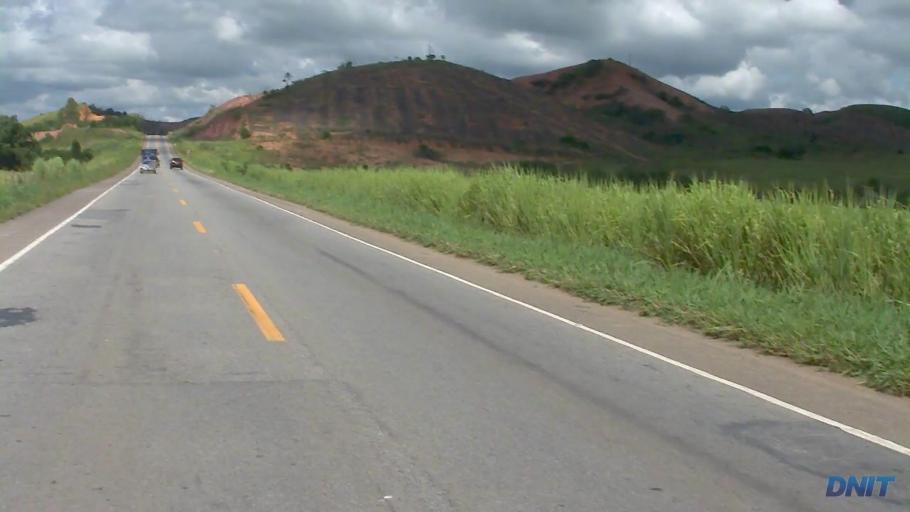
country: BR
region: Minas Gerais
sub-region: Belo Oriente
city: Belo Oriente
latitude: -19.1424
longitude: -42.2251
